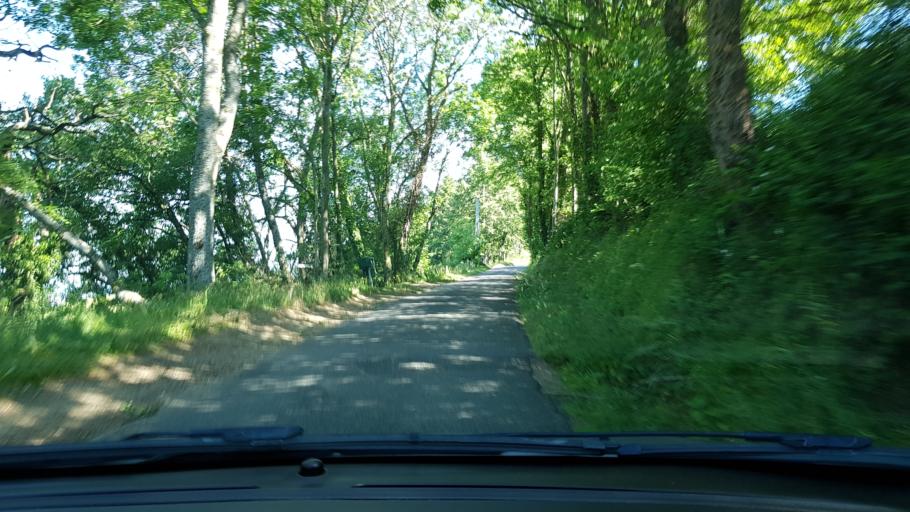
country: FR
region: Rhone-Alpes
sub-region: Departement du Rhone
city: Saint-Didier-sous-Riverie
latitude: 45.5884
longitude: 4.5897
